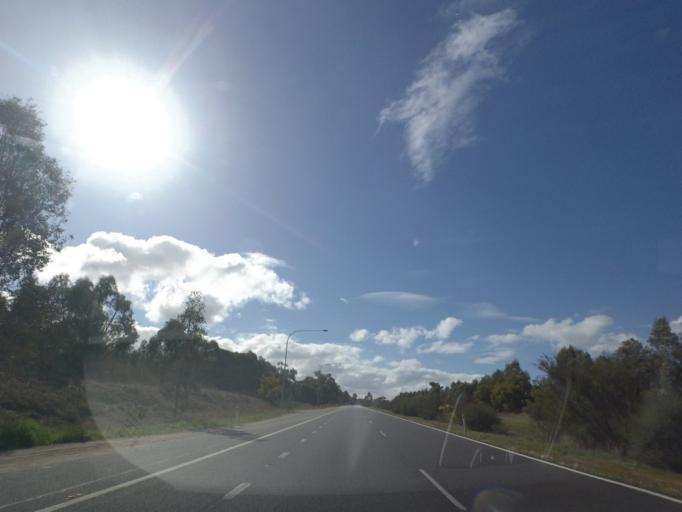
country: AU
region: New South Wales
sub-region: Albury Municipality
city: Lavington
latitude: -36.0343
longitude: 146.9757
